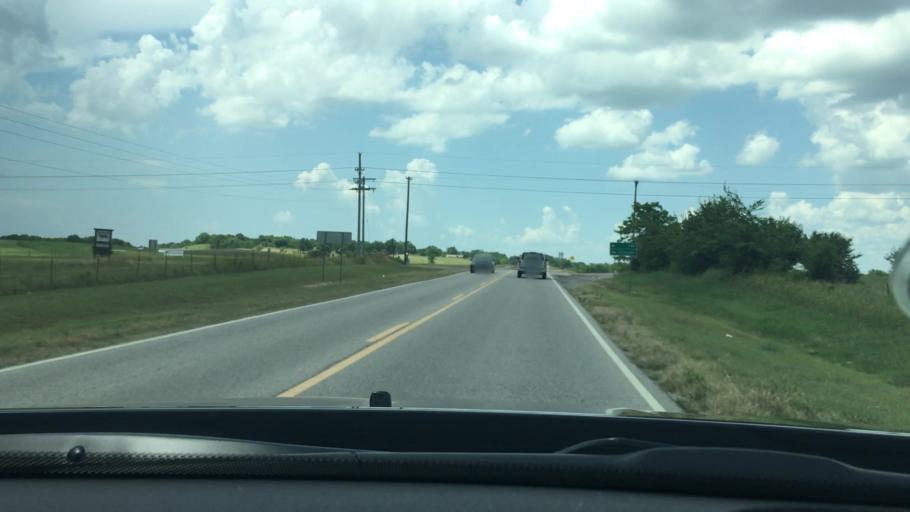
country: US
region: Oklahoma
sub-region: Pontotoc County
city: Ada
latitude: 34.7225
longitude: -96.6348
